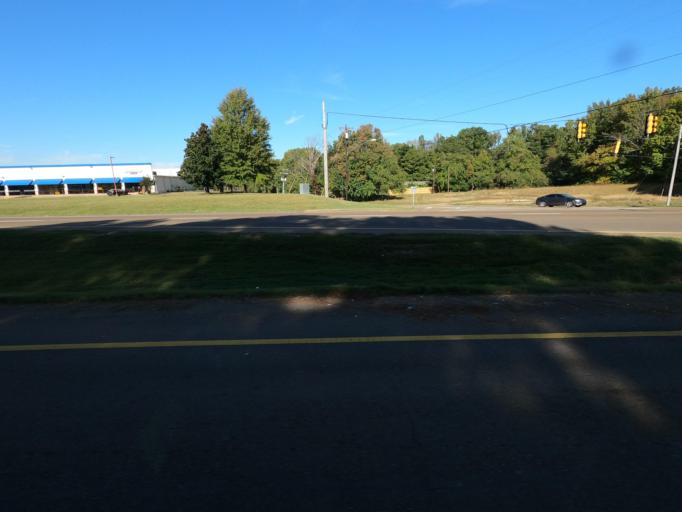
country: US
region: Tennessee
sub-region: Tipton County
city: Brighton
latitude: 35.4833
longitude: -89.7394
